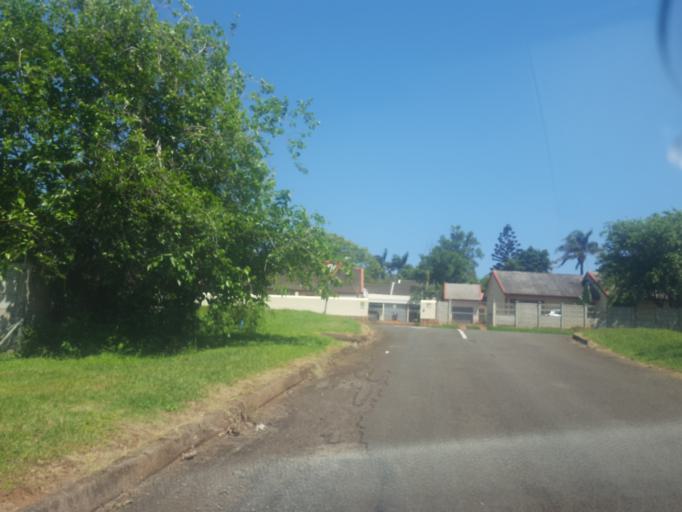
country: ZA
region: KwaZulu-Natal
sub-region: uThungulu District Municipality
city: Empangeni
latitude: -28.7572
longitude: 31.9061
